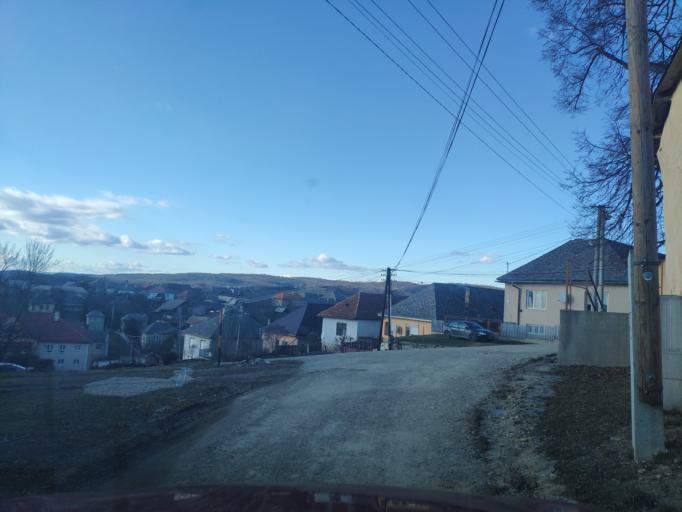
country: SK
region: Kosicky
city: Roznava
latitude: 48.5550
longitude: 20.5244
